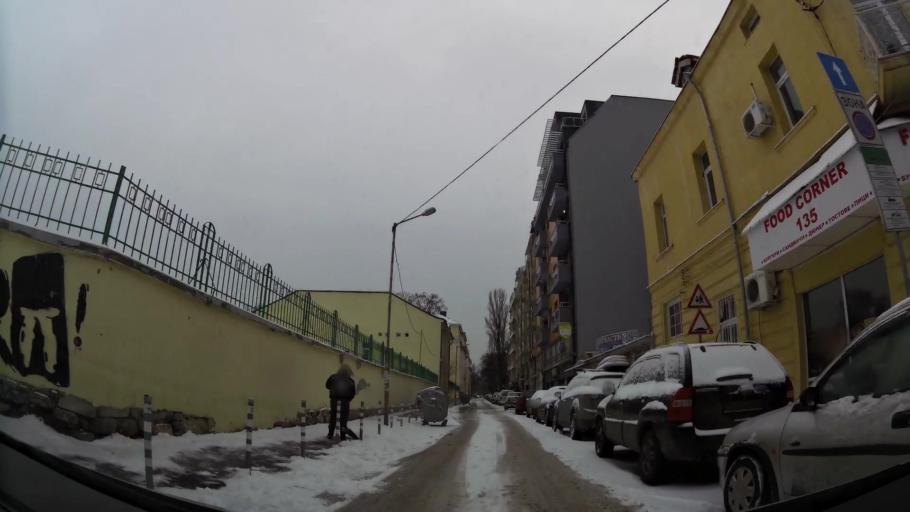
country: BG
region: Sofia-Capital
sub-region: Stolichna Obshtina
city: Sofia
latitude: 42.7029
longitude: 23.3119
